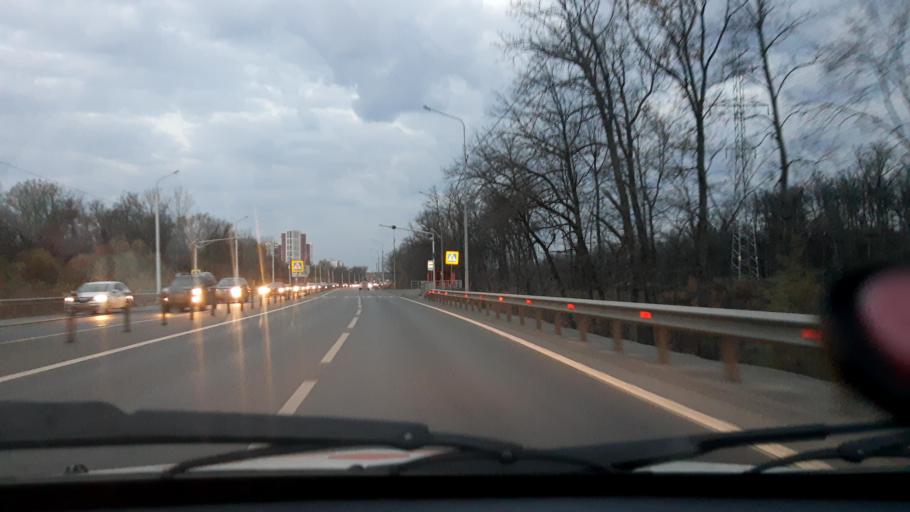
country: RU
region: Bashkortostan
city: Ufa
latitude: 54.6993
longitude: 55.8810
